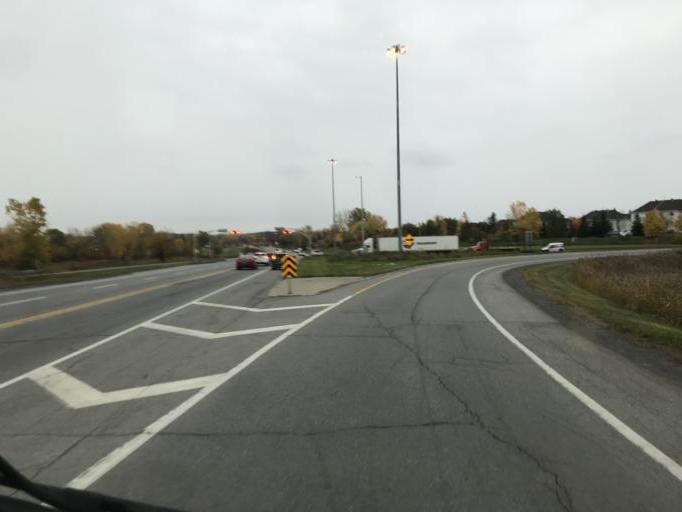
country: CA
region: Quebec
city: Bois-des-Filion
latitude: 45.6714
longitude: -73.7647
